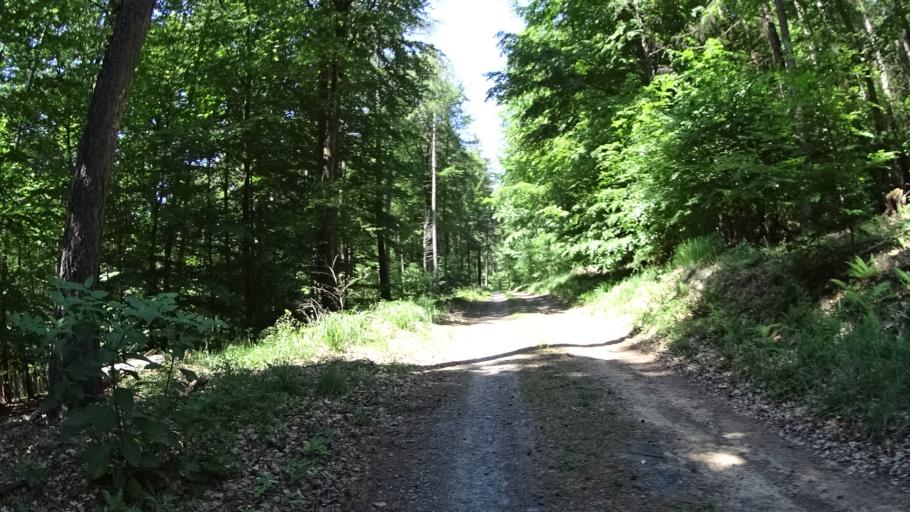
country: DE
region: Baden-Wuerttemberg
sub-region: Karlsruhe Region
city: Schonau
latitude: 49.4295
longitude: 8.7816
